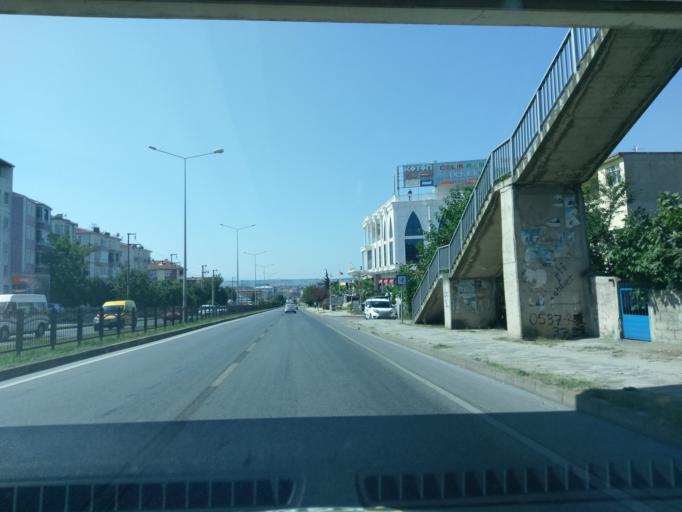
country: TR
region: Samsun
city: Bafra
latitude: 41.5565
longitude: 35.9107
